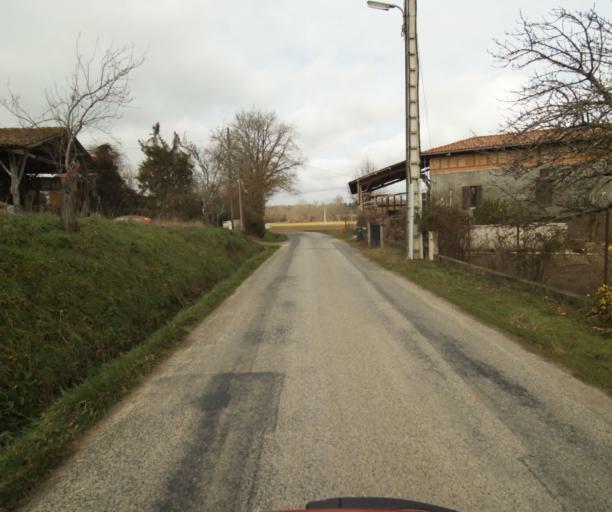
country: FR
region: Midi-Pyrenees
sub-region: Departement de l'Ariege
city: Pamiers
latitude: 43.1045
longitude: 1.5506
